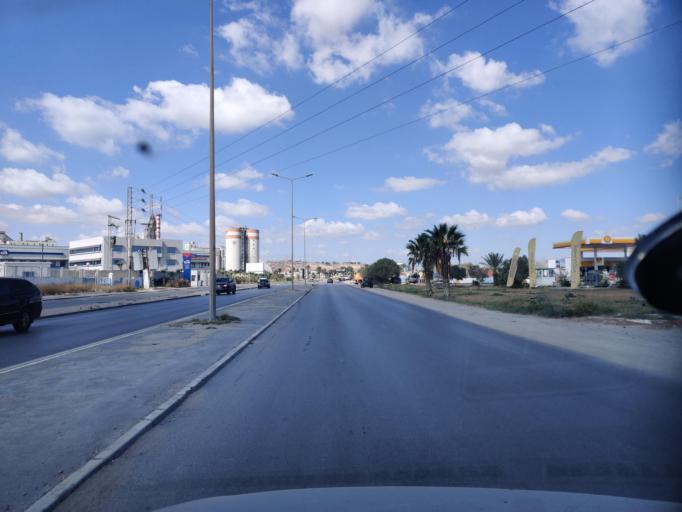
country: TN
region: Bin 'Arus
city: Ben Arous
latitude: 36.7770
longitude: 10.2096
